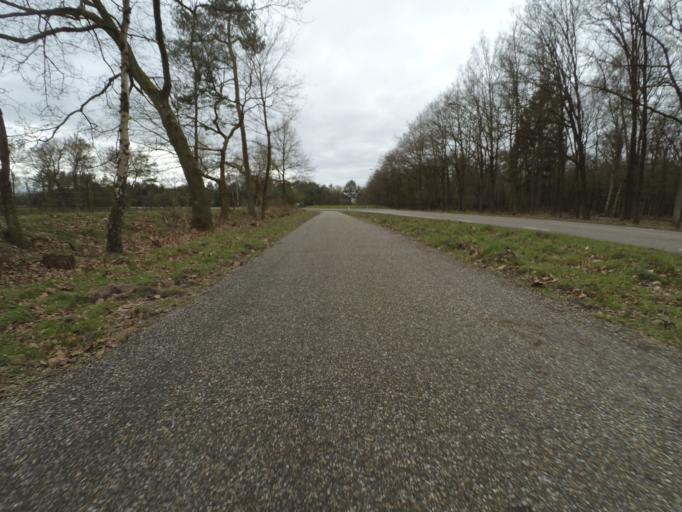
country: NL
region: Gelderland
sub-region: Gemeente Apeldoorn
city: Beekbergen
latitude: 52.1024
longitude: 5.9520
